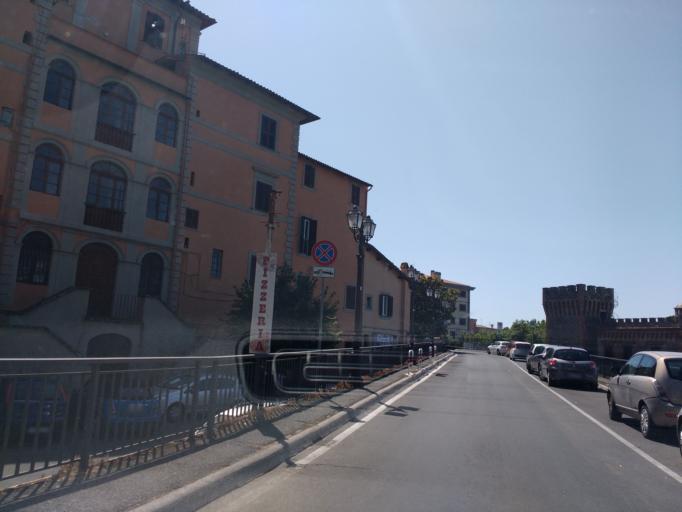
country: IT
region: Latium
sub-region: Citta metropolitana di Roma Capitale
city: Rocca di Papa
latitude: 41.7626
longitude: 12.7071
